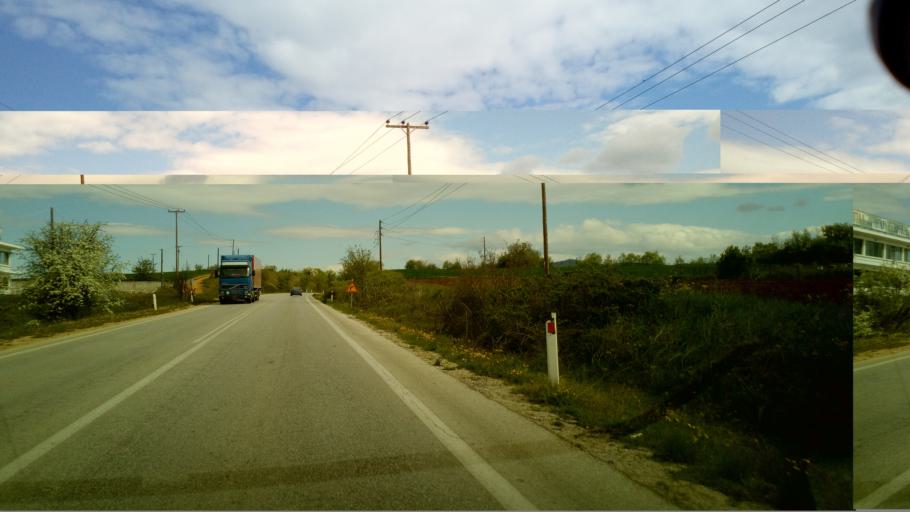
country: GR
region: Central Macedonia
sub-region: Nomos Thessalonikis
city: Drymos
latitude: 40.7821
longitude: 22.9443
